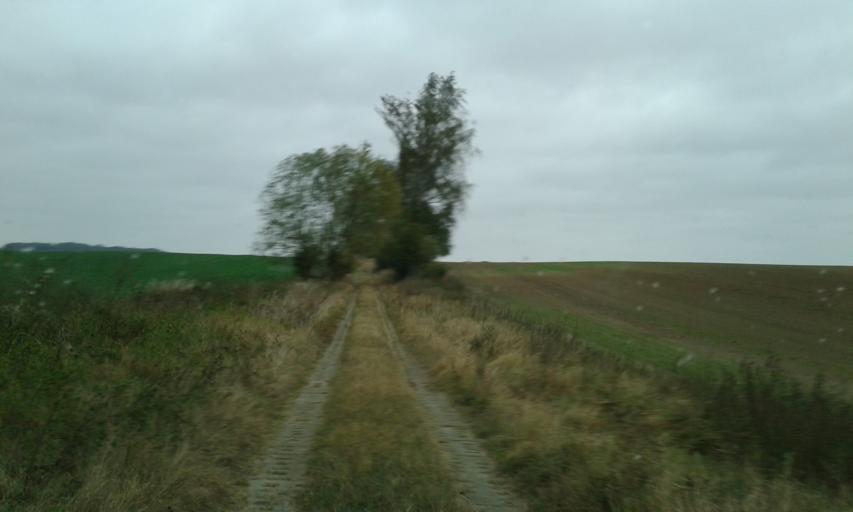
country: PL
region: West Pomeranian Voivodeship
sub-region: Powiat stargardzki
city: Dolice
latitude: 53.1159
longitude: 15.2108
